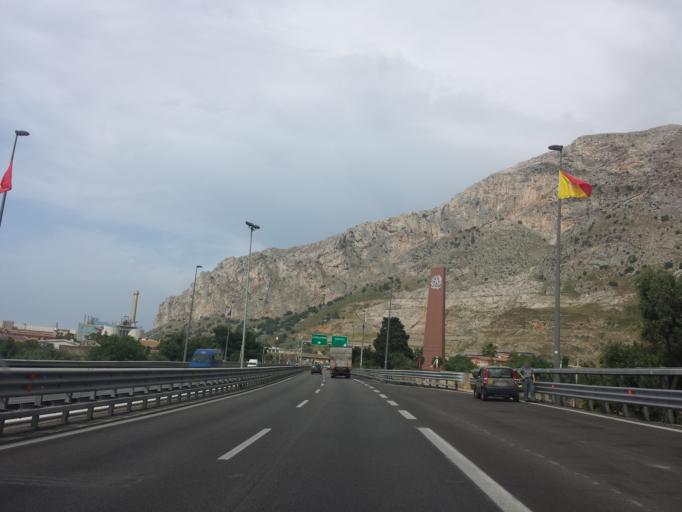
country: IT
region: Sicily
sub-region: Palermo
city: Isola delle Femmine
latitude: 38.1831
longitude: 13.2456
